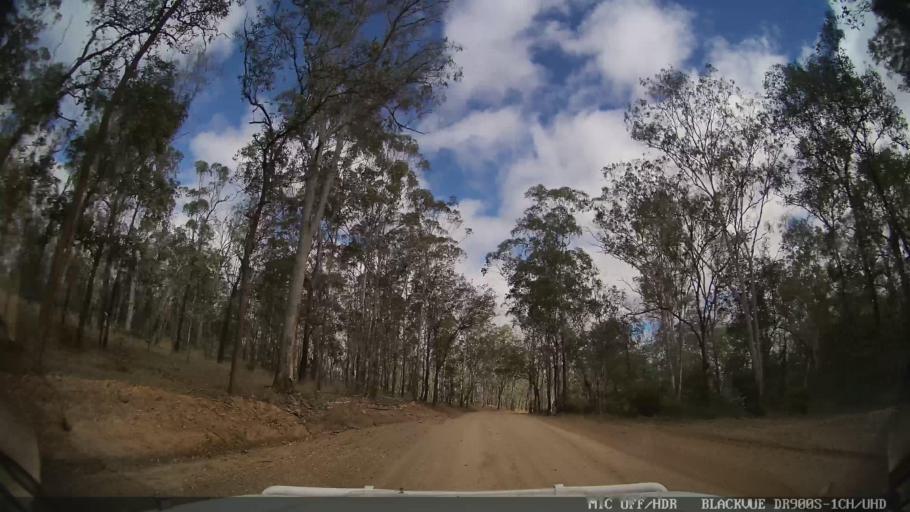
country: AU
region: Queensland
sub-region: Gladstone
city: Toolooa
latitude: -24.6849
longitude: 151.3288
